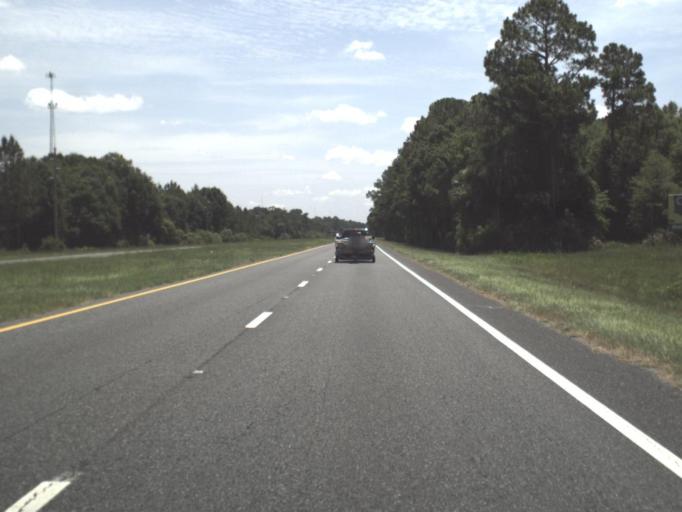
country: US
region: Florida
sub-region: Dixie County
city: Cross City
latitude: 29.6528
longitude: -83.1731
